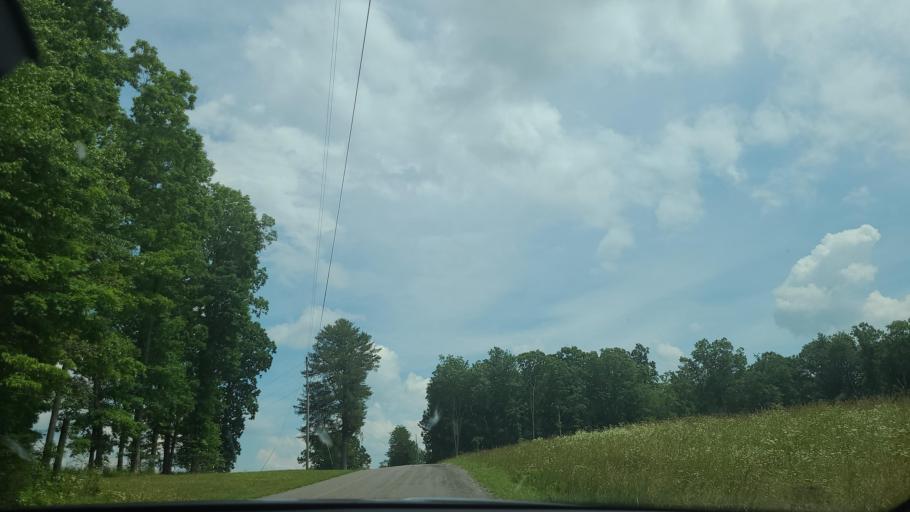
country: US
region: Tennessee
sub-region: Cumberland County
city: Lake Tansi
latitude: 35.7749
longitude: -85.0621
